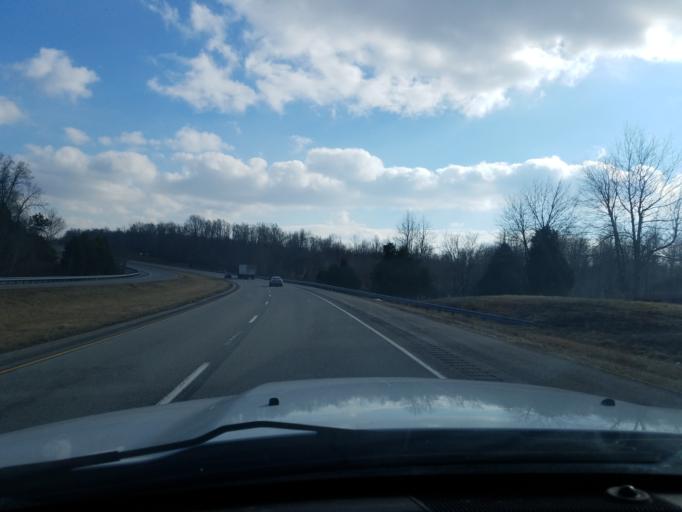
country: US
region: Kentucky
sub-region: Hardin County
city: Elizabethtown
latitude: 37.6420
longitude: -85.8381
